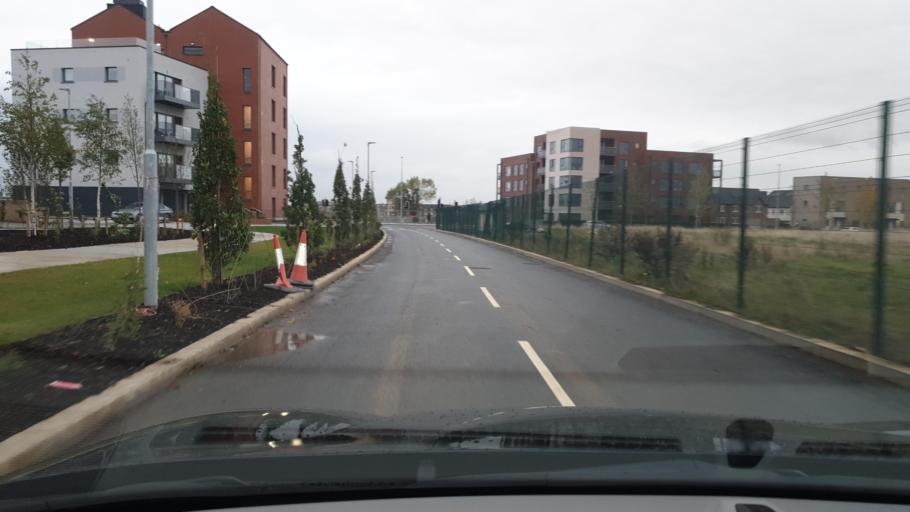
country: IE
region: Leinster
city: Lucan
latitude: 53.3431
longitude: -6.4656
